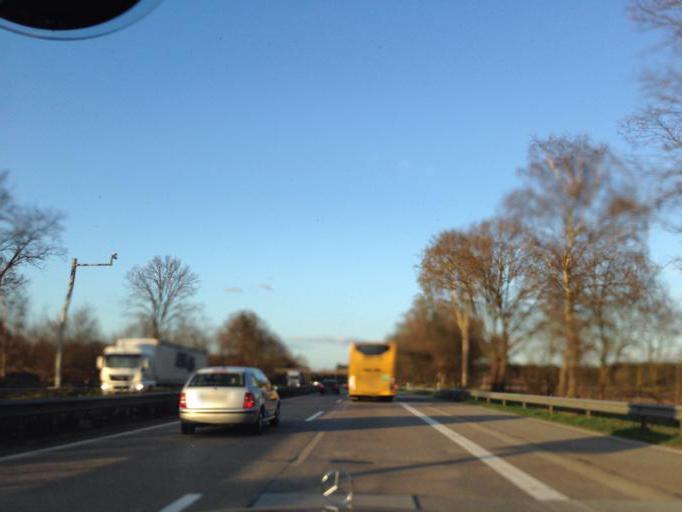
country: DE
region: Lower Saxony
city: Soltau
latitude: 52.9363
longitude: 9.8536
